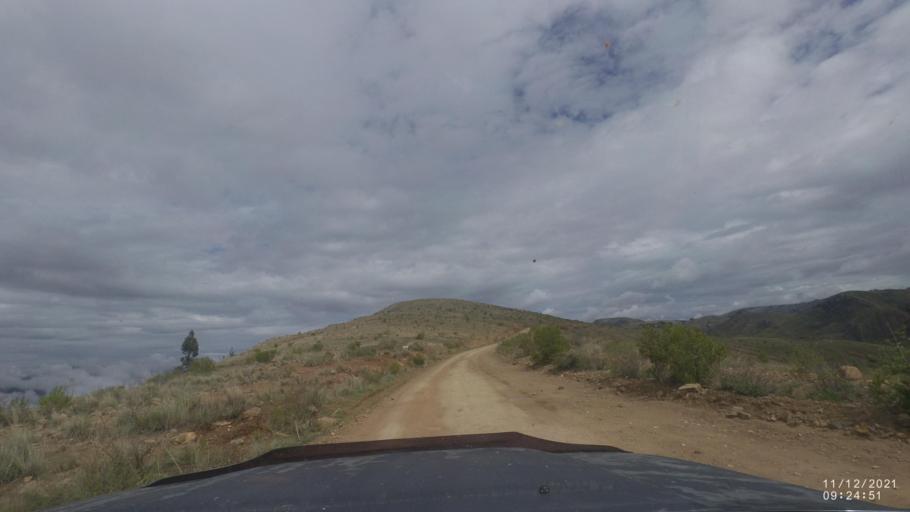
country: BO
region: Cochabamba
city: Tarata
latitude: -17.8734
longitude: -65.9825
